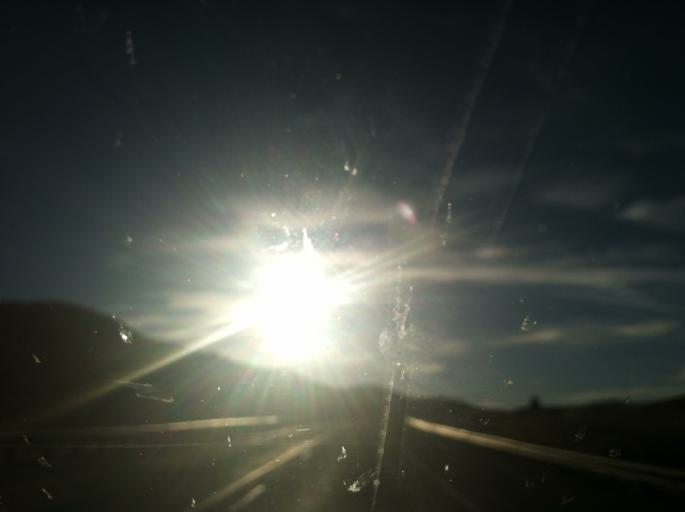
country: US
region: Montana
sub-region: Granite County
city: Philipsburg
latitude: 46.6969
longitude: -113.2243
